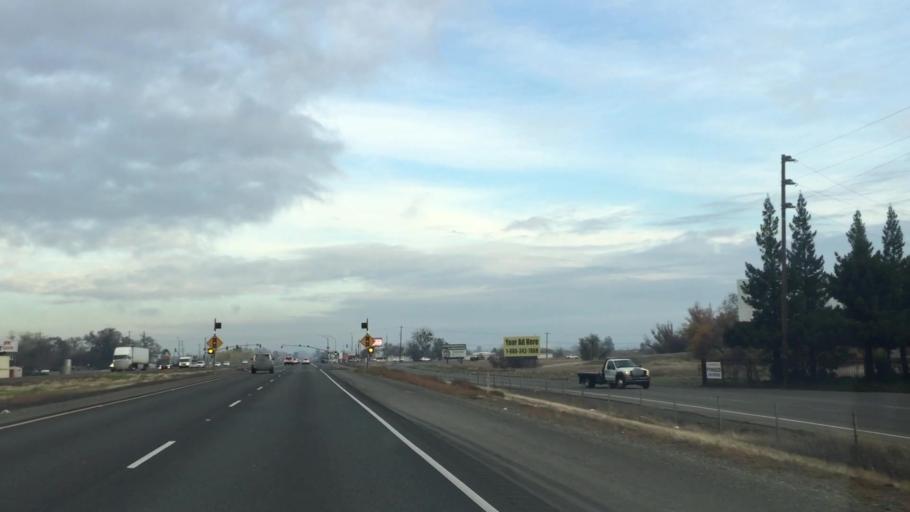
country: US
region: California
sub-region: Butte County
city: South Oroville
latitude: 39.4740
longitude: -121.5756
